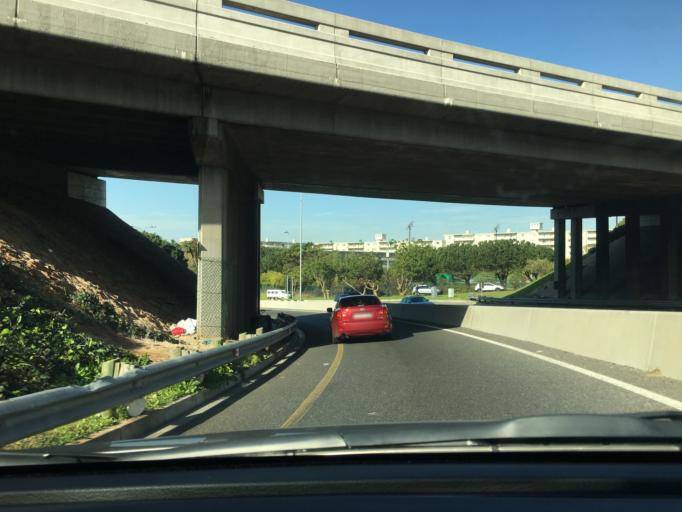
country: ZA
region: Western Cape
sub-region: City of Cape Town
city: Rosebank
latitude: -33.9462
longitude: 18.4665
